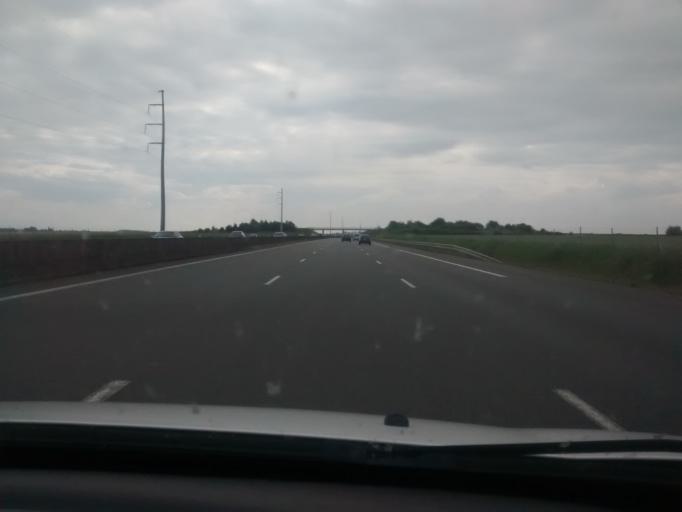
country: FR
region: Centre
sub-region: Departement d'Eure-et-Loir
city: Bailleau-le-Pin
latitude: 48.3316
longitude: 1.3878
